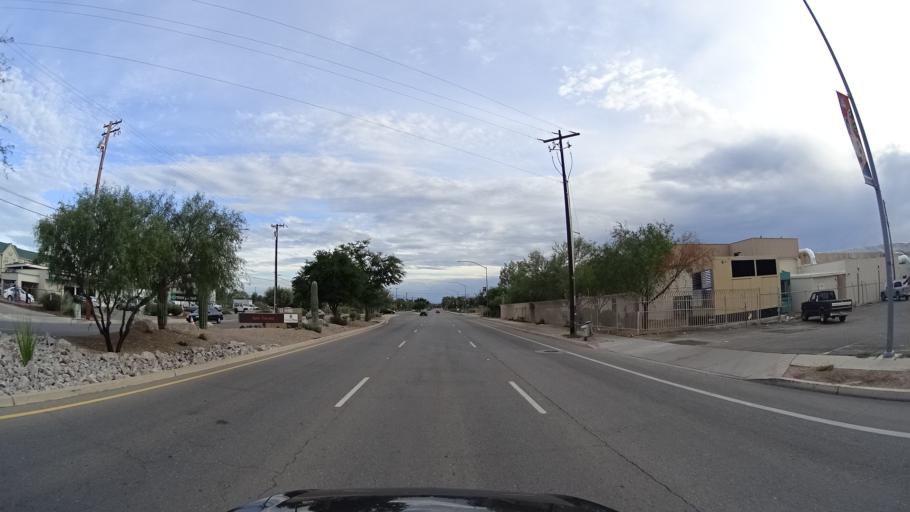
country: US
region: Arizona
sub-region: Pima County
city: Summit
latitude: 32.1316
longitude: -110.9347
